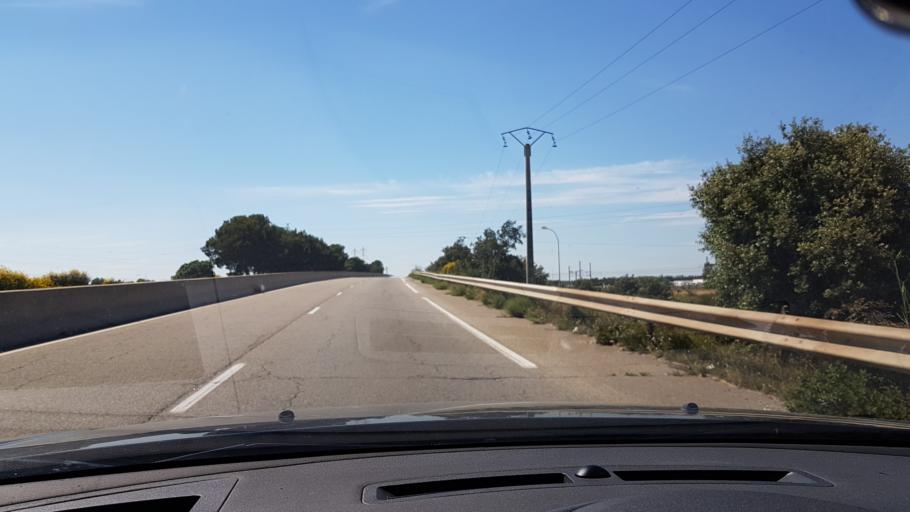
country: FR
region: Provence-Alpes-Cote d'Azur
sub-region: Departement des Bouches-du-Rhone
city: Fos-sur-Mer
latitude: 43.4725
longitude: 4.9056
